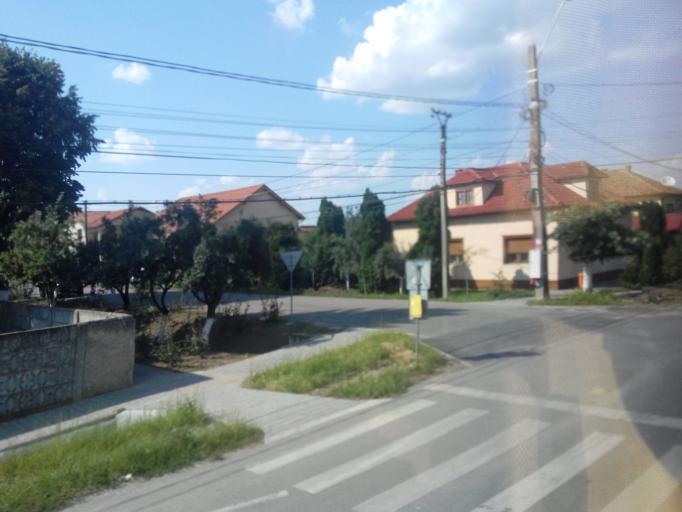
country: RO
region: Timis
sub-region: Comuna Dumbravita
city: Dumbravita
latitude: 45.7972
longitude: 21.2426
